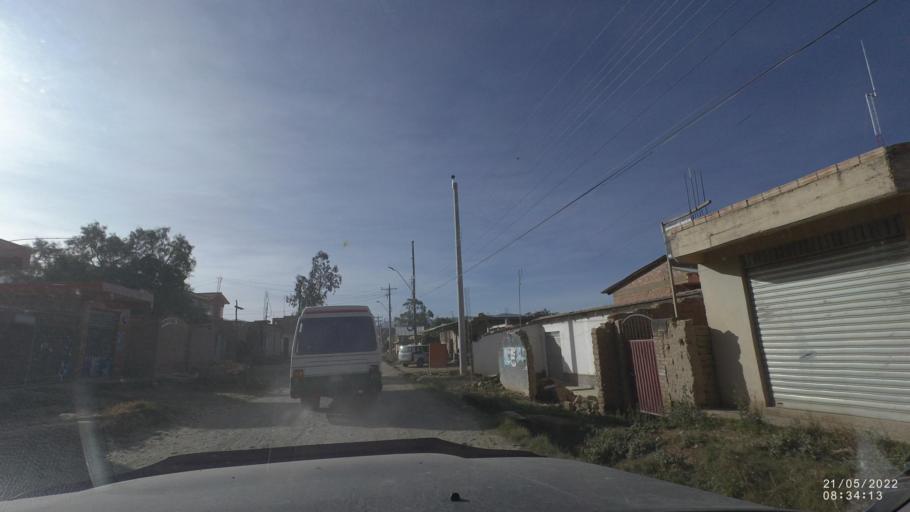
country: BO
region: Cochabamba
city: Cochabamba
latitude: -17.3870
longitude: -66.0468
